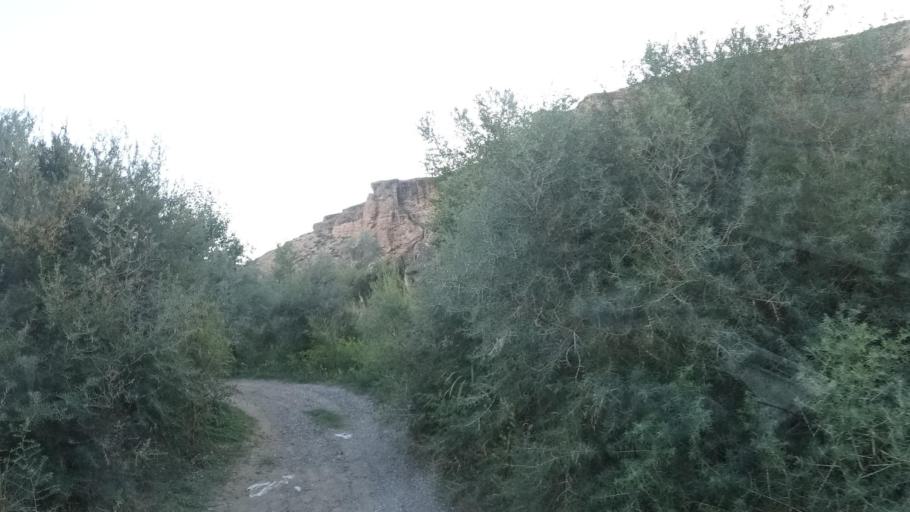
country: KZ
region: Almaty Oblysy
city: Kegen
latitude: 43.2740
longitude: 78.9770
